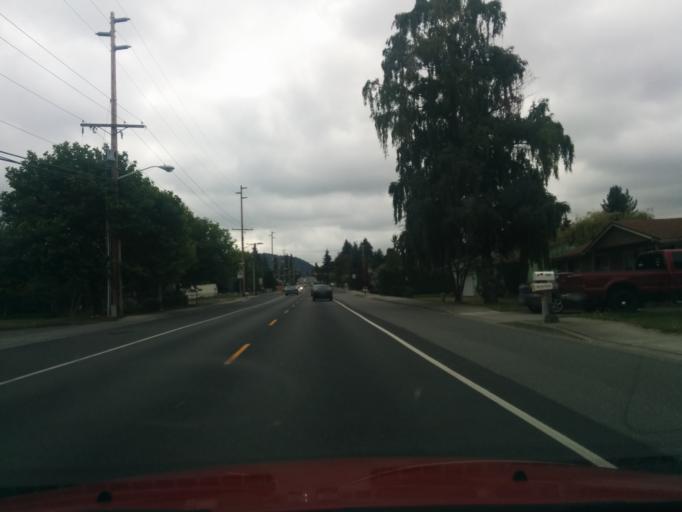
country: US
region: Washington
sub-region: Skagit County
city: Mount Vernon
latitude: 48.4307
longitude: -122.3134
